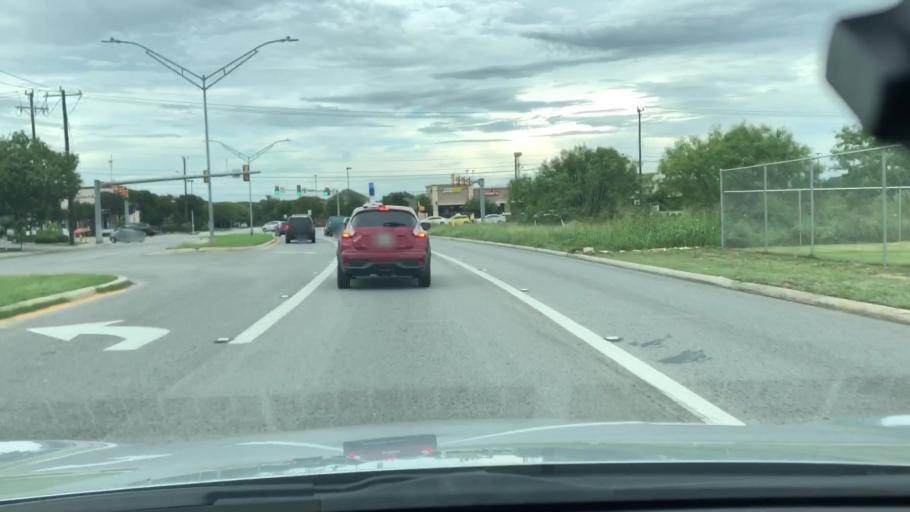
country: US
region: Texas
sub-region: Bexar County
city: Leon Valley
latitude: 29.4772
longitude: -98.6641
